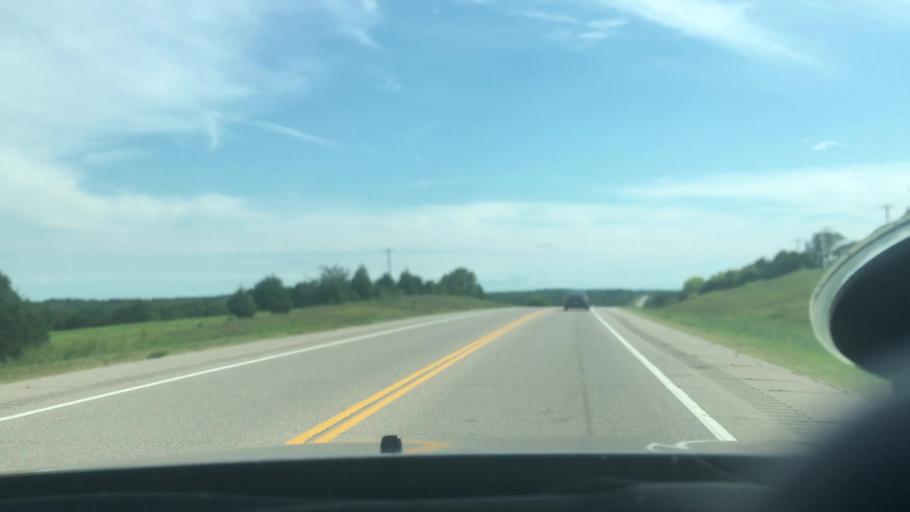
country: US
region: Oklahoma
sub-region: Seminole County
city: Konawa
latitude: 35.0389
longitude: -96.6784
